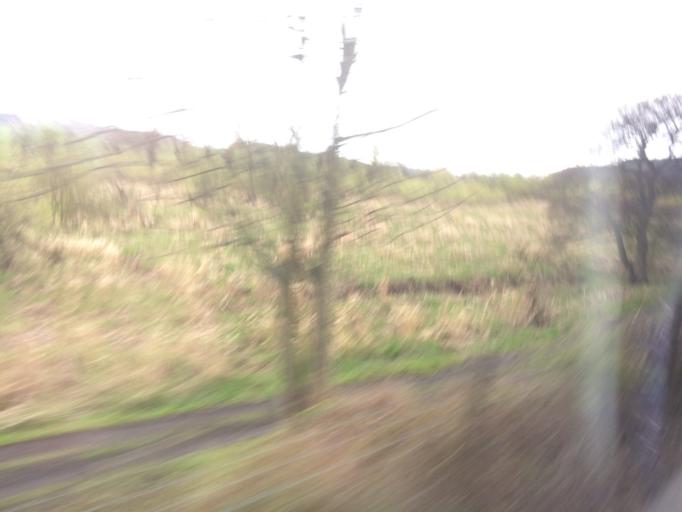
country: GB
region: Scotland
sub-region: Perth and Kinross
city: Bridge of Earn
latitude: 56.3817
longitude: -3.3638
